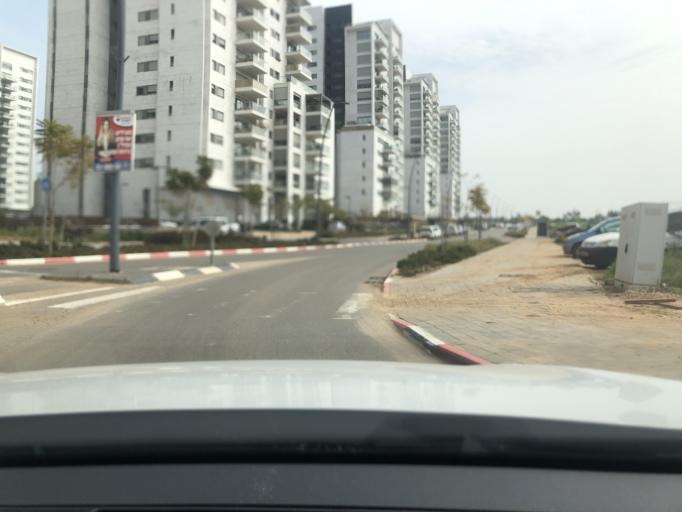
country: IL
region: Central District
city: Rosh Ha'Ayin
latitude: 32.1056
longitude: 34.9455
